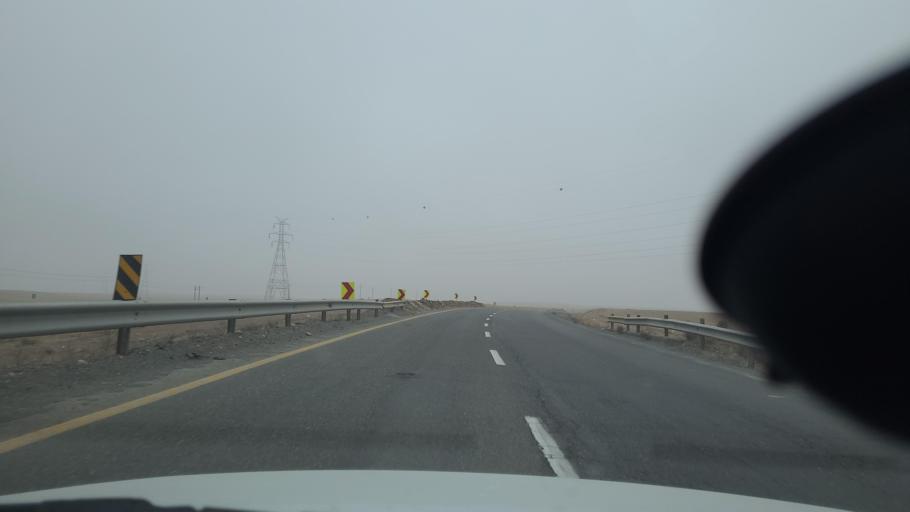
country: IR
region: Razavi Khorasan
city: Fariman
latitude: 35.8673
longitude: 59.7620
